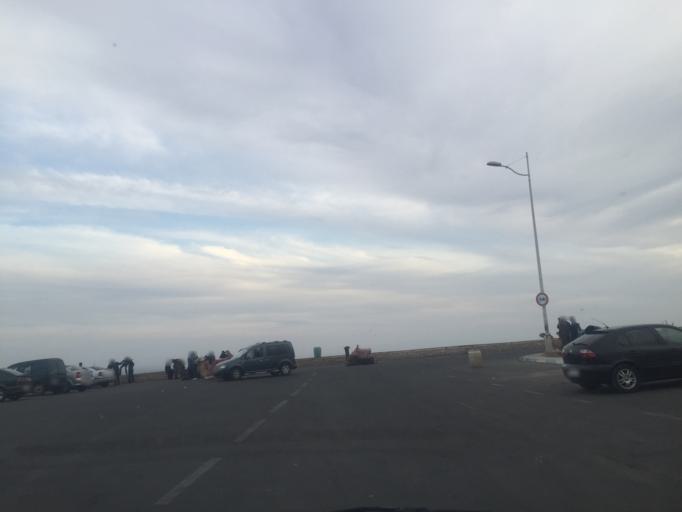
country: MA
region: Souss-Massa-Draa
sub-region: Agadir-Ida-ou-Tnan
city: Agadir
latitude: 30.4297
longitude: -9.6237
